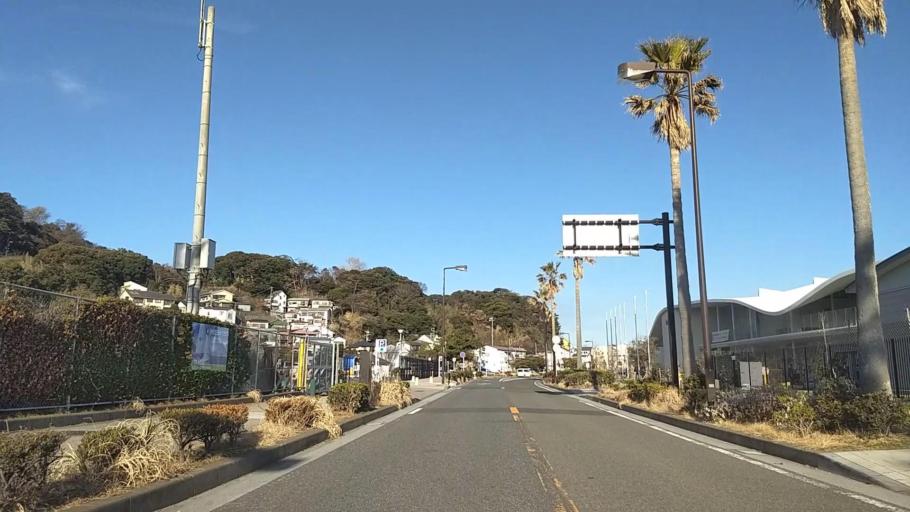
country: JP
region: Kanagawa
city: Fujisawa
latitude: 35.2989
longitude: 139.4837
